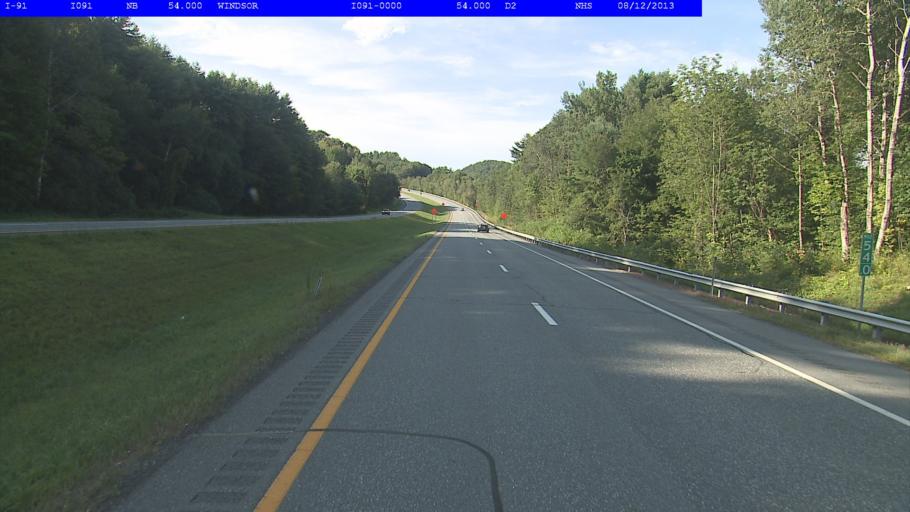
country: US
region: Vermont
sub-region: Windsor County
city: Windsor
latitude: 43.4378
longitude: -72.4026
